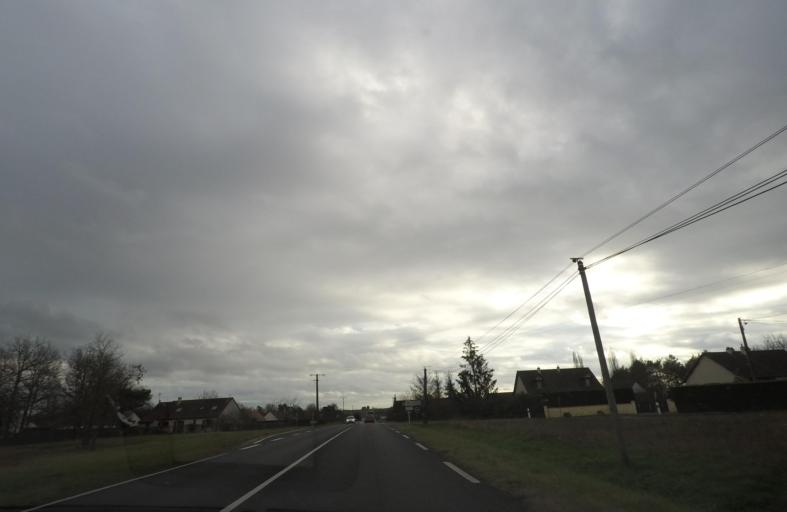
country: FR
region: Centre
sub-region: Departement du Loir-et-Cher
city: Mur-de-Sologne
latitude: 47.4169
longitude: 1.5967
